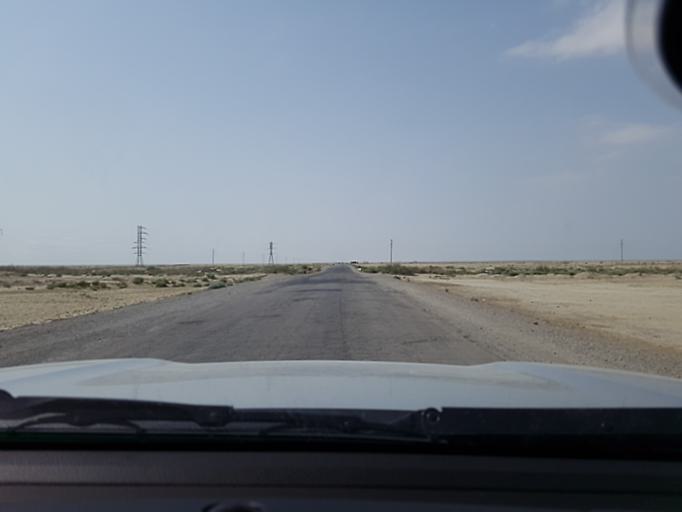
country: TM
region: Balkan
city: Gumdag
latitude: 39.0041
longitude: 54.5860
